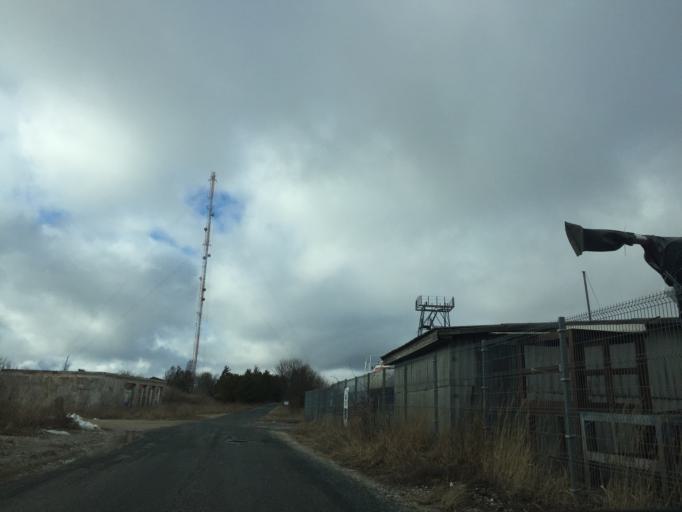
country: EE
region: Laeaene
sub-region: Haapsalu linn
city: Haapsalu
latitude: 58.9594
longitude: 23.5225
